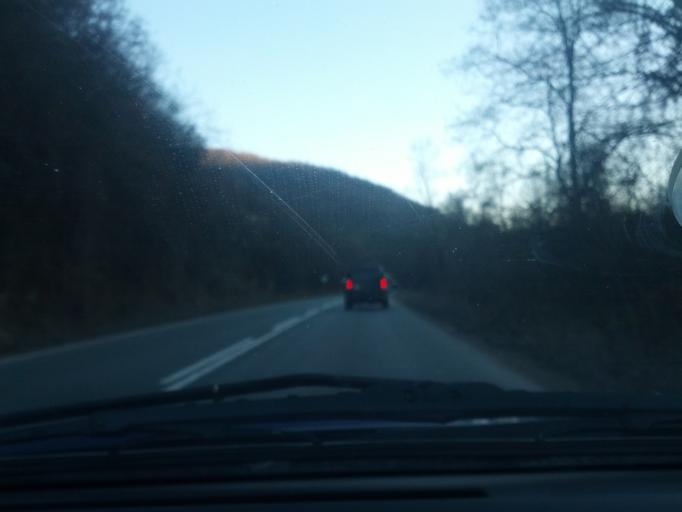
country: BG
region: Vratsa
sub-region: Obshtina Mezdra
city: Mezdra
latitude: 43.0978
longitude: 23.6843
